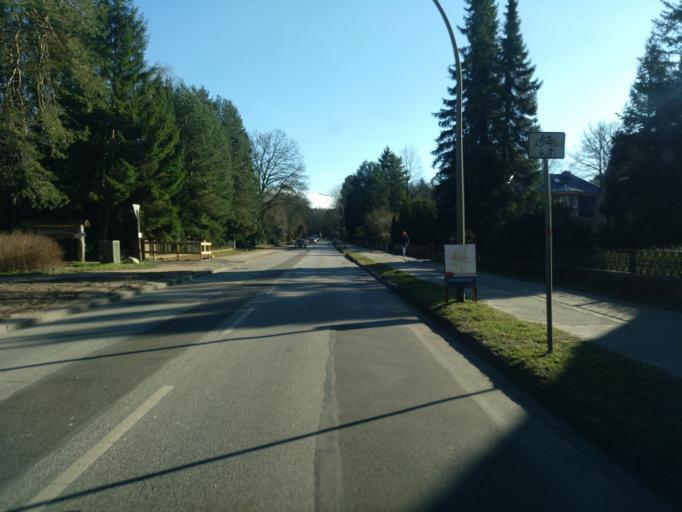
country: DE
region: Lower Saxony
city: Neu Wulmstorf
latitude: 53.4670
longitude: 9.8893
